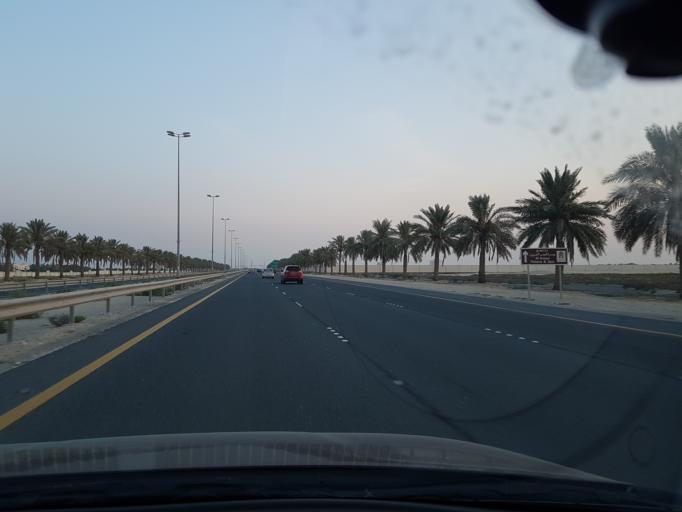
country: BH
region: Central Governorate
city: Dar Kulayb
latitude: 26.0450
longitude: 50.4998
